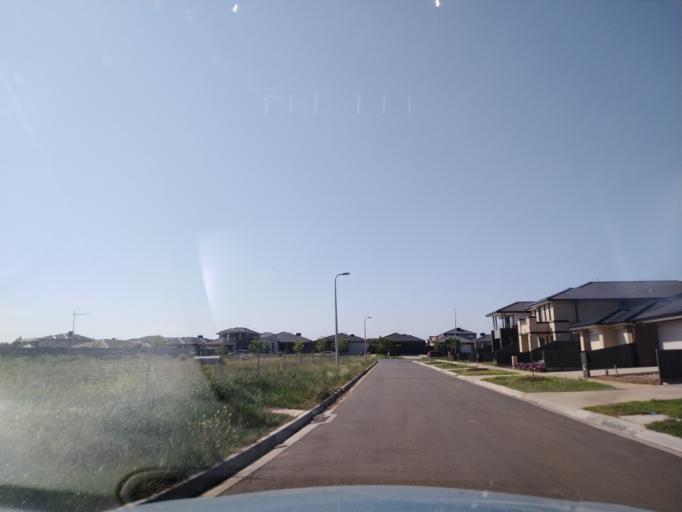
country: AU
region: Victoria
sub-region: Wyndham
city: Williams Landing
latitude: -37.8453
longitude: 144.7418
